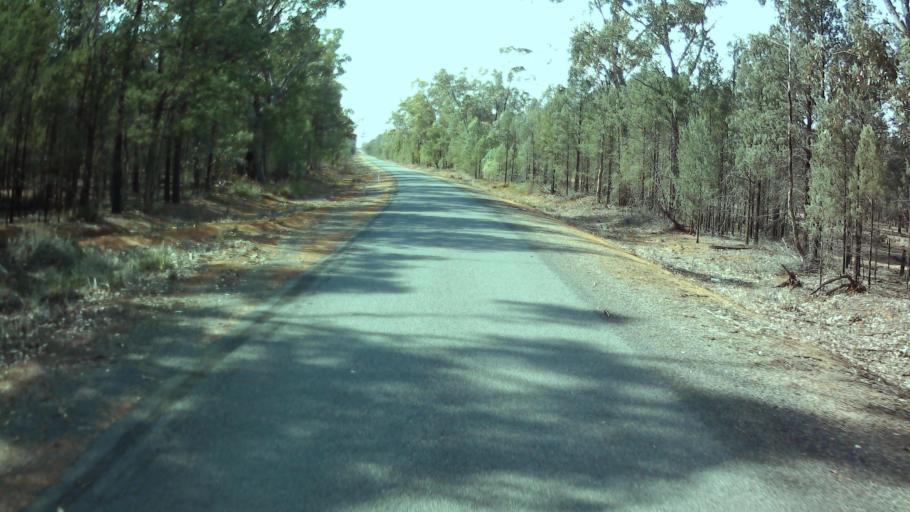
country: AU
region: New South Wales
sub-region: Weddin
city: Grenfell
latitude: -33.7237
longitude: 148.0298
